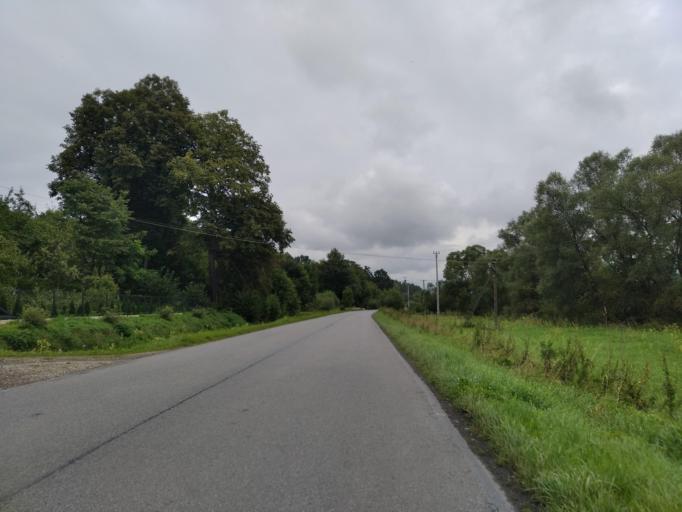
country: PL
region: Subcarpathian Voivodeship
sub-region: Powiat przemyski
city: Bircza
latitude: 49.6921
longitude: 22.3912
